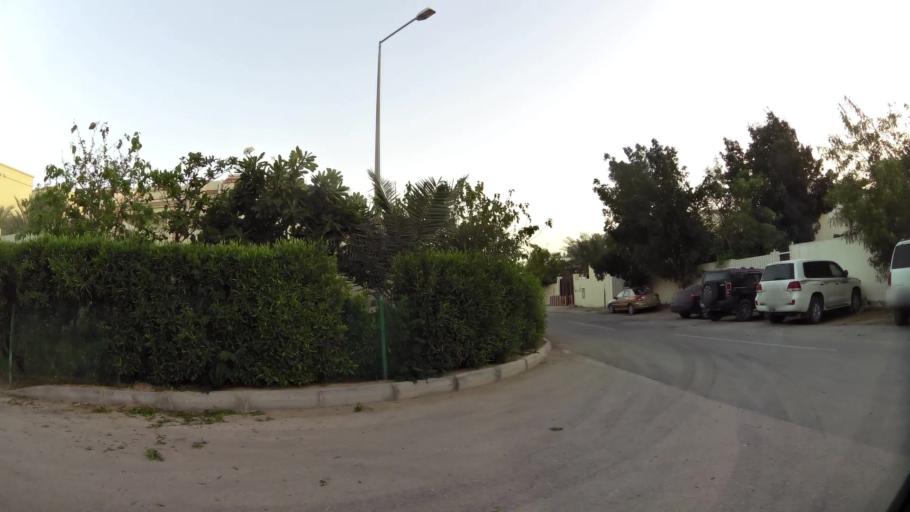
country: QA
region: Baladiyat ar Rayyan
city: Ar Rayyan
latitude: 25.3256
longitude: 51.4617
